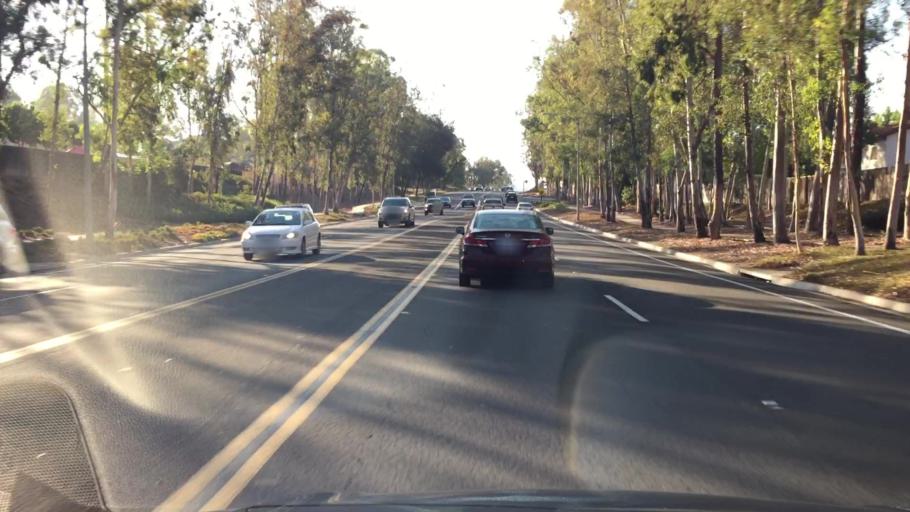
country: US
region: California
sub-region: San Diego County
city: Poway
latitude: 32.9769
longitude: -117.0475
